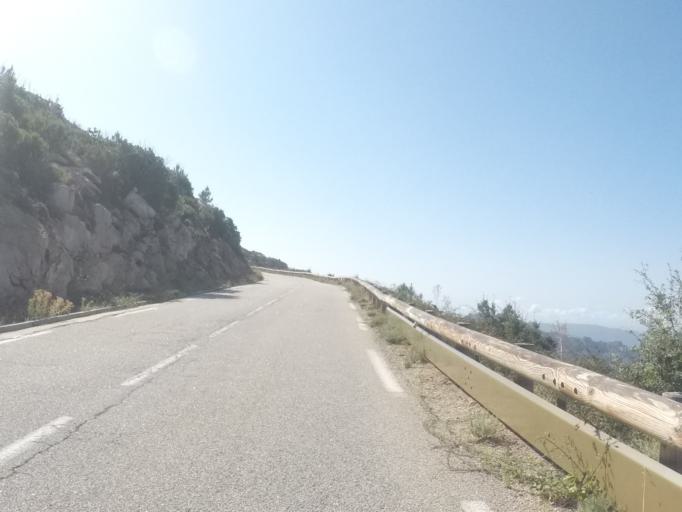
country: FR
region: Corsica
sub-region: Departement de la Corse-du-Sud
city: Olmeto
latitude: 41.7683
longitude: 9.0271
